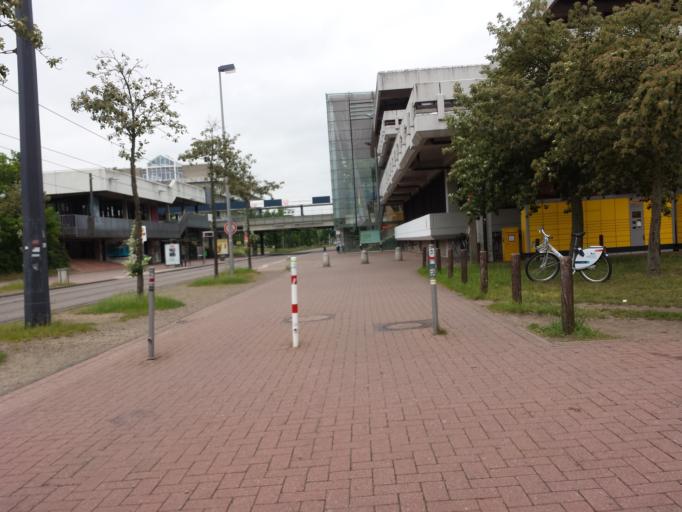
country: DE
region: Bremen
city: Bremen
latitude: 53.1071
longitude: 8.8520
